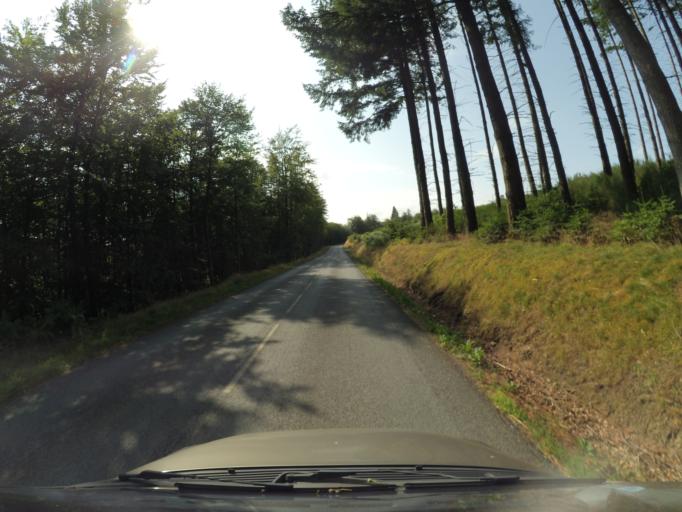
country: FR
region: Limousin
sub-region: Departement de la Correze
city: Meymac
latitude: 45.6345
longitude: 2.1006
